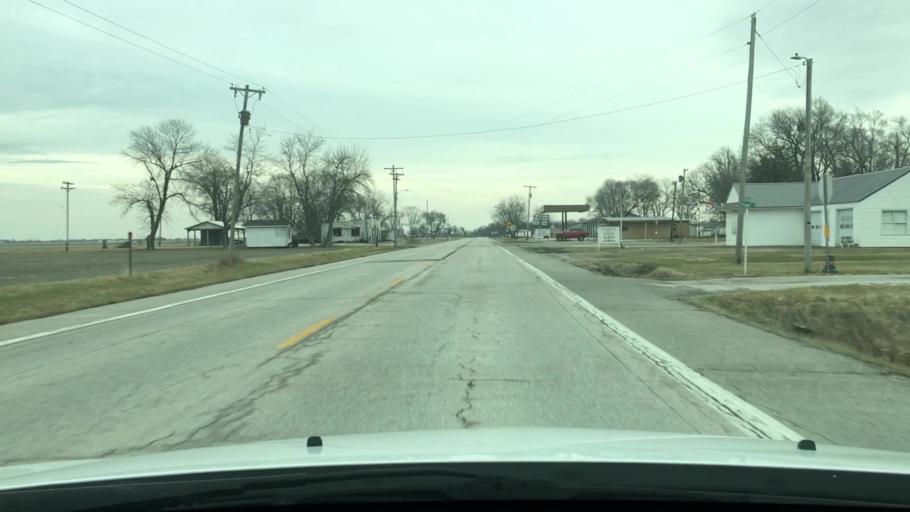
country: US
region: Missouri
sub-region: Audrain County
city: Vandalia
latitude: 39.2793
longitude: -91.5777
